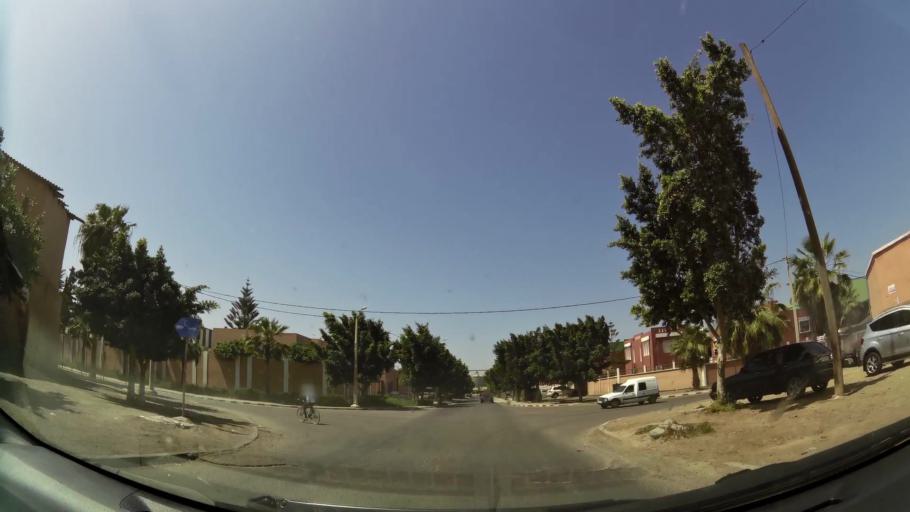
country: MA
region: Souss-Massa-Draa
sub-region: Inezgane-Ait Mellou
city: Inezgane
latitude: 30.3268
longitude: -9.4881
